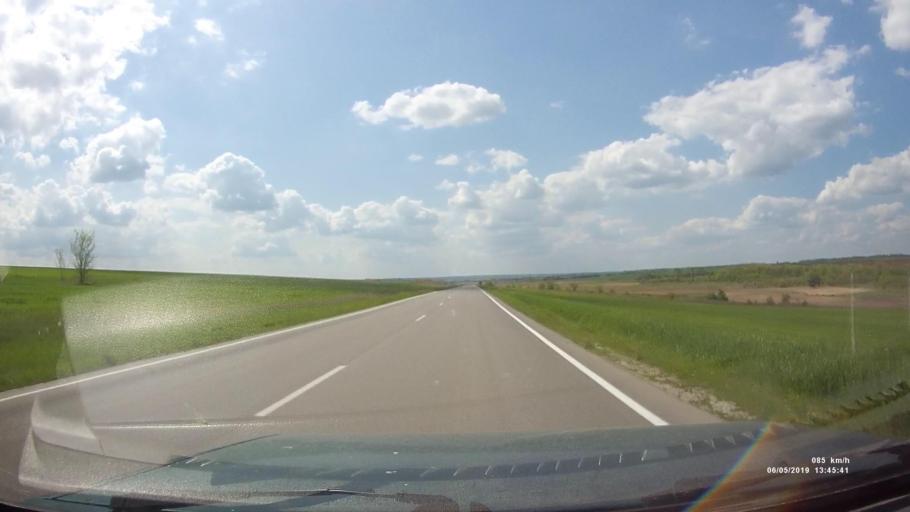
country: RU
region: Rostov
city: Melikhovskaya
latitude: 47.6573
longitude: 40.5958
